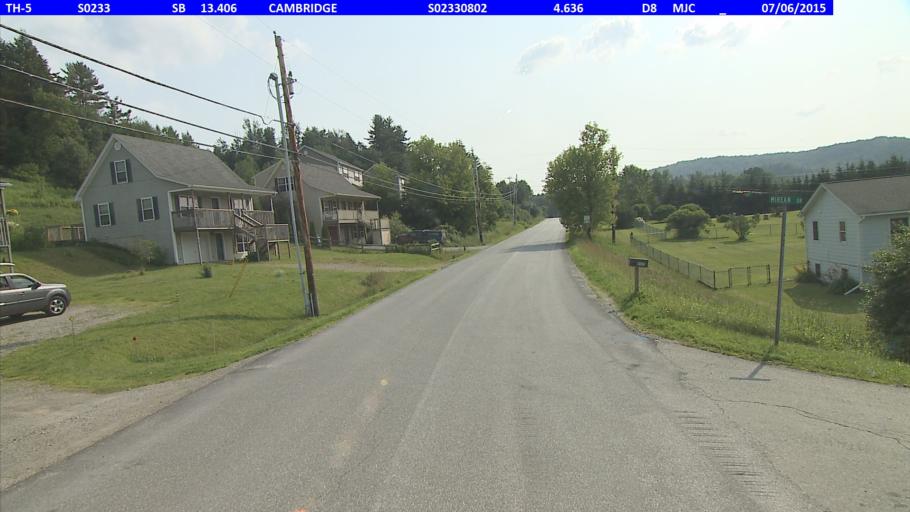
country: US
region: Vermont
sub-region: Lamoille County
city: Johnson
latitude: 44.6418
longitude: -72.8319
